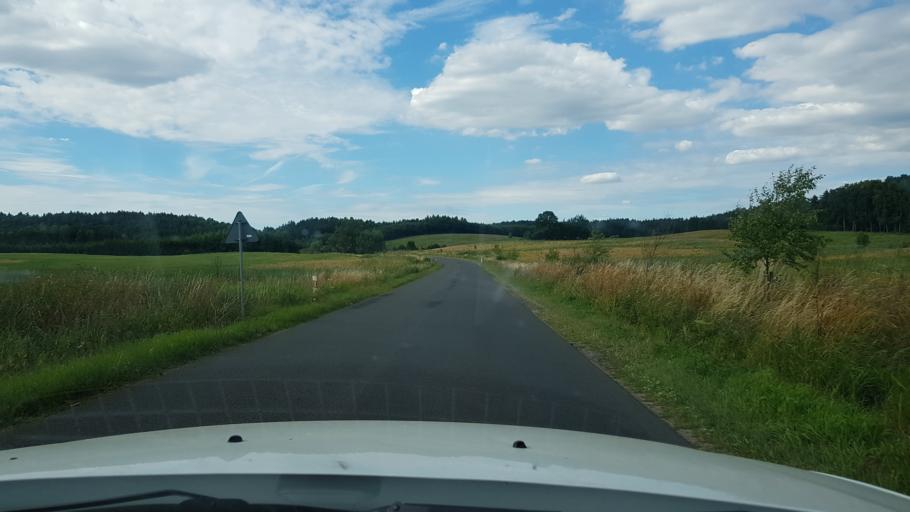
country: PL
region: West Pomeranian Voivodeship
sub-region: Powiat drawski
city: Wierzchowo
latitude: 53.4835
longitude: 16.0451
